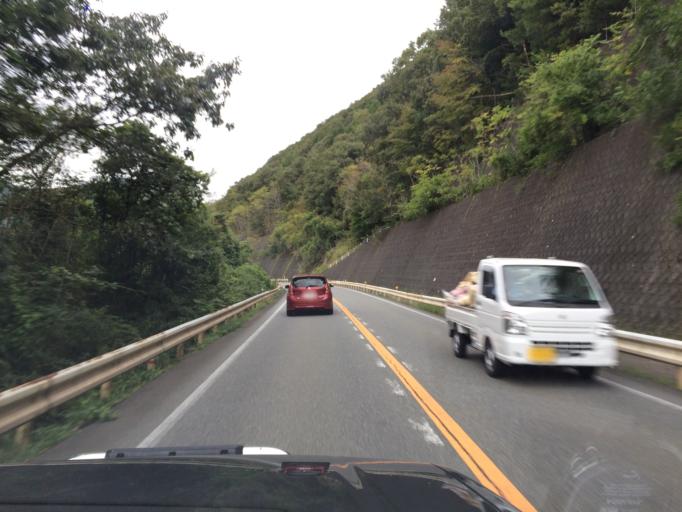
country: JP
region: Hyogo
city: Toyooka
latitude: 35.3682
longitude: 134.8216
